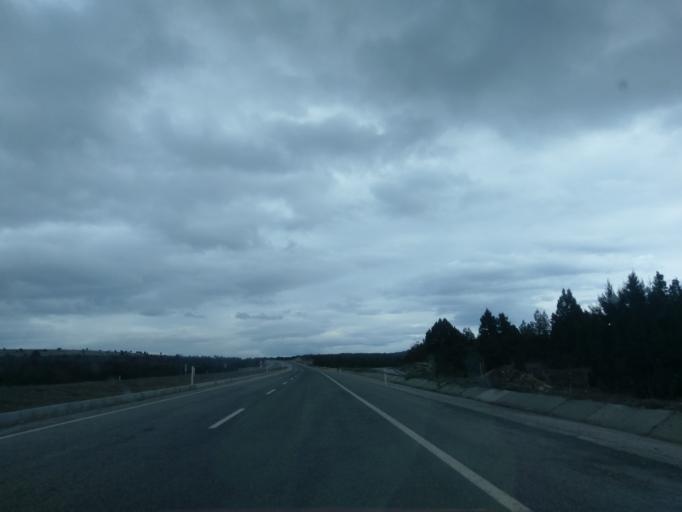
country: TR
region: Kuetahya
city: Aslanapa
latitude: 39.2228
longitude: 29.7447
